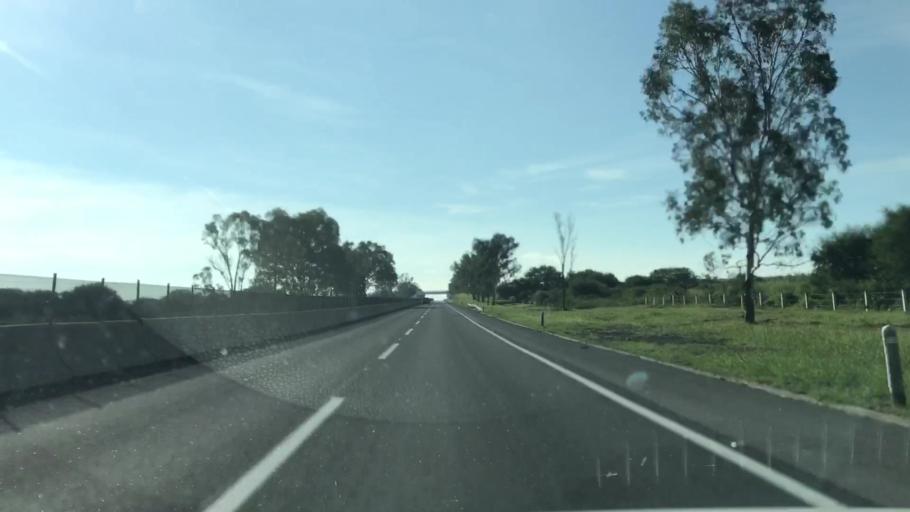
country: MX
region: Jalisco
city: Encarnacion de Diaz
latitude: 21.4596
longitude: -102.2106
